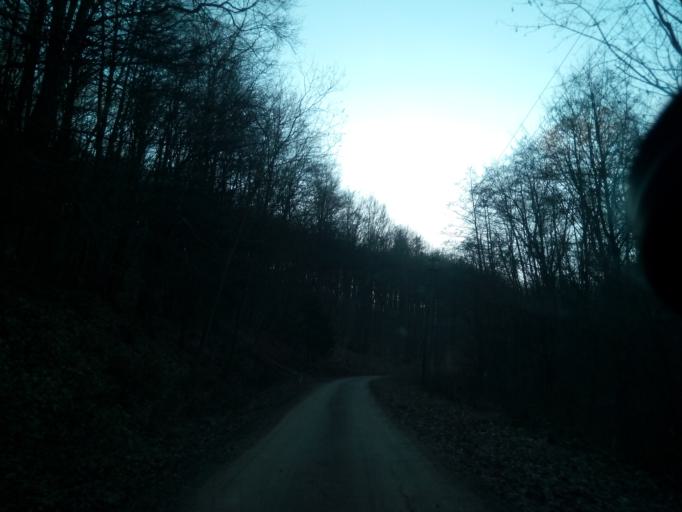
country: SK
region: Kosicky
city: Medzev
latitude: 48.6768
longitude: 20.8799
